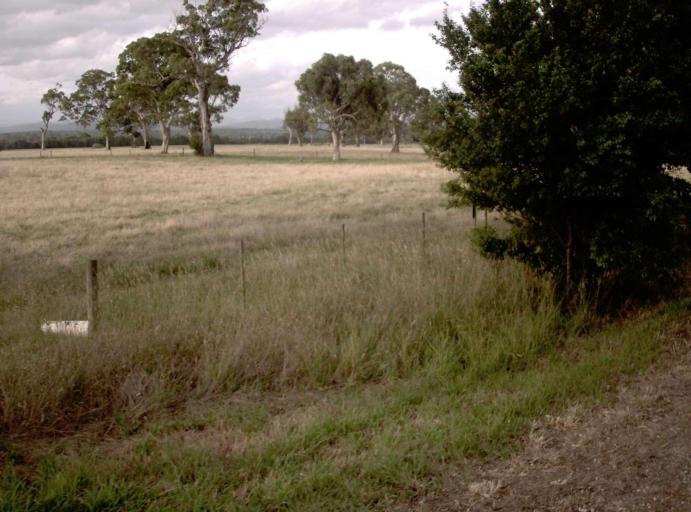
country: AU
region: Victoria
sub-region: Wellington
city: Sale
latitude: -37.8604
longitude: 147.0368
